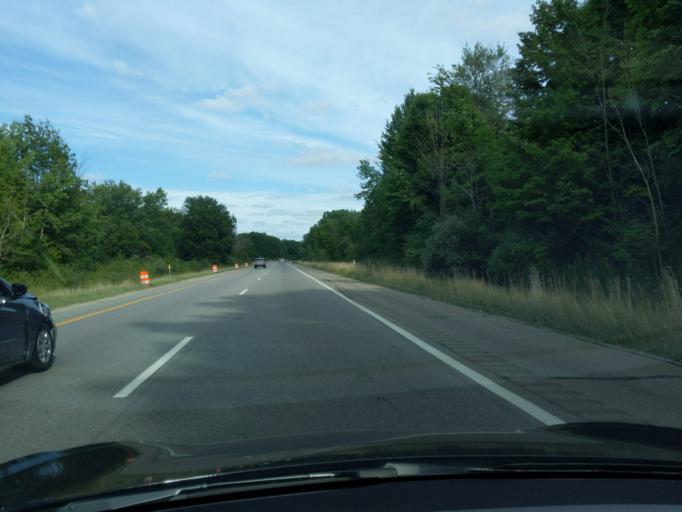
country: US
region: Michigan
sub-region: Ottawa County
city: Coopersville
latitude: 43.0734
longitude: -86.0481
